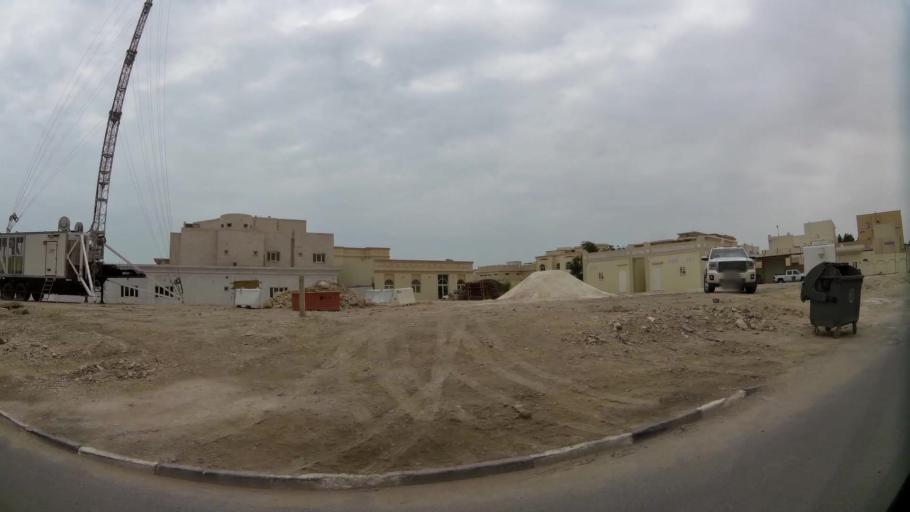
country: QA
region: Baladiyat ar Rayyan
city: Ar Rayyan
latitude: 25.3439
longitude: 51.4597
